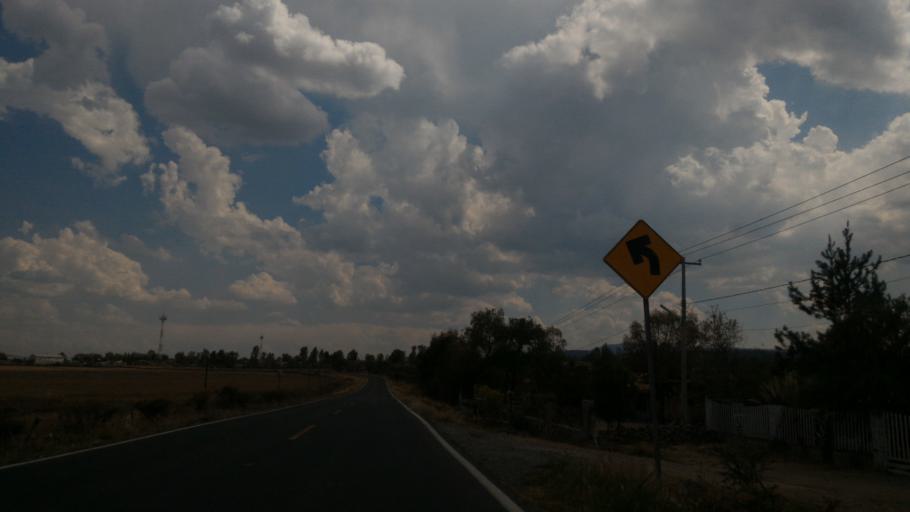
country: MX
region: Guanajuato
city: Ciudad Manuel Doblado
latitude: 20.8093
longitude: -101.9976
